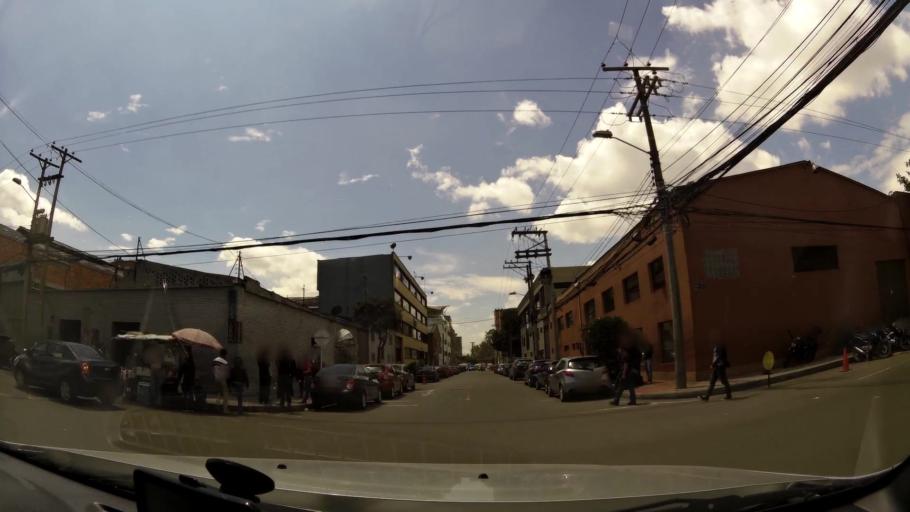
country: CO
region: Bogota D.C.
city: Bogota
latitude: 4.6287
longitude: -74.1001
